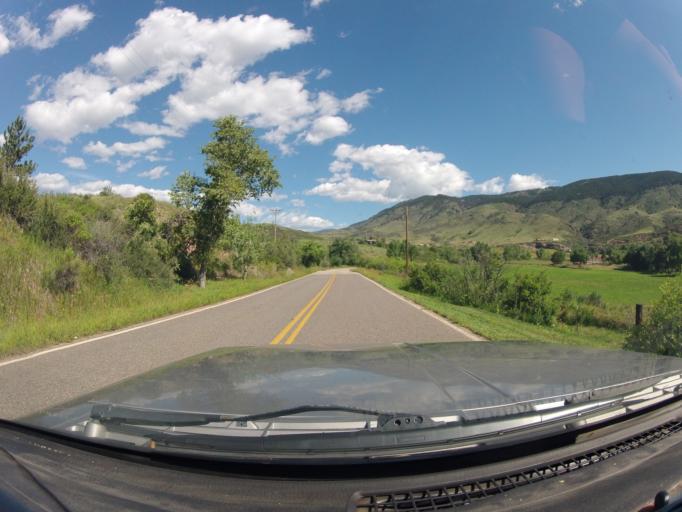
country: US
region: Colorado
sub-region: Larimer County
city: Laporte
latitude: 40.5129
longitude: -105.2519
